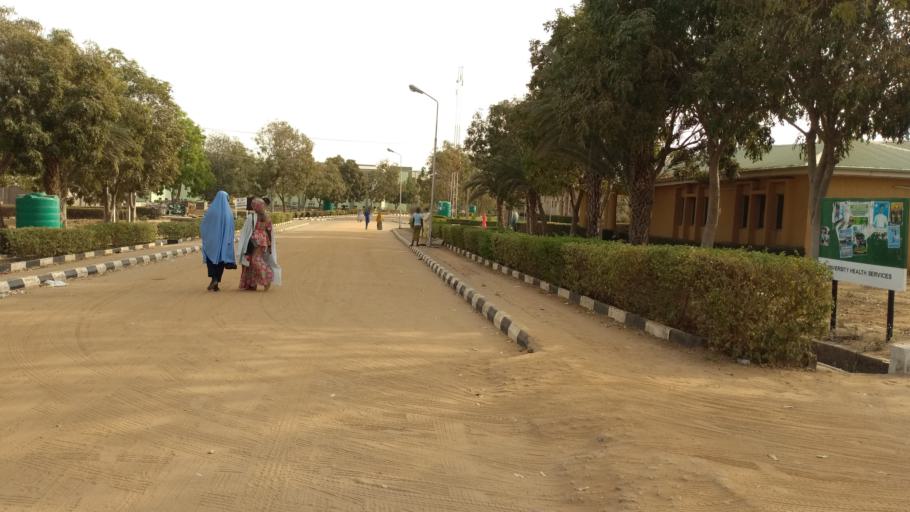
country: NG
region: Gombe
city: Gombe
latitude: 10.3068
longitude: 11.1750
